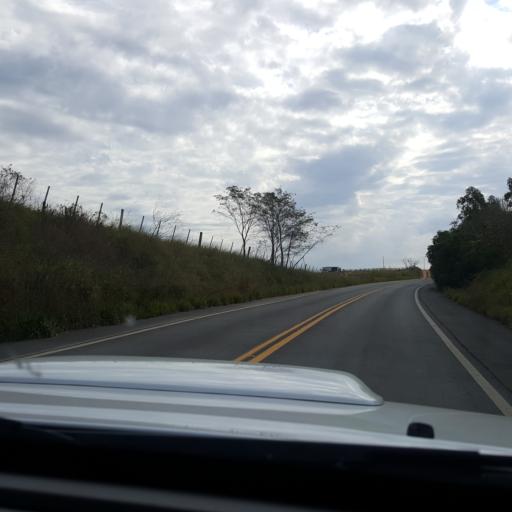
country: BR
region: Sao Paulo
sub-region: Itaporanga
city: Itaporanga
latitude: -23.7693
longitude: -49.4444
